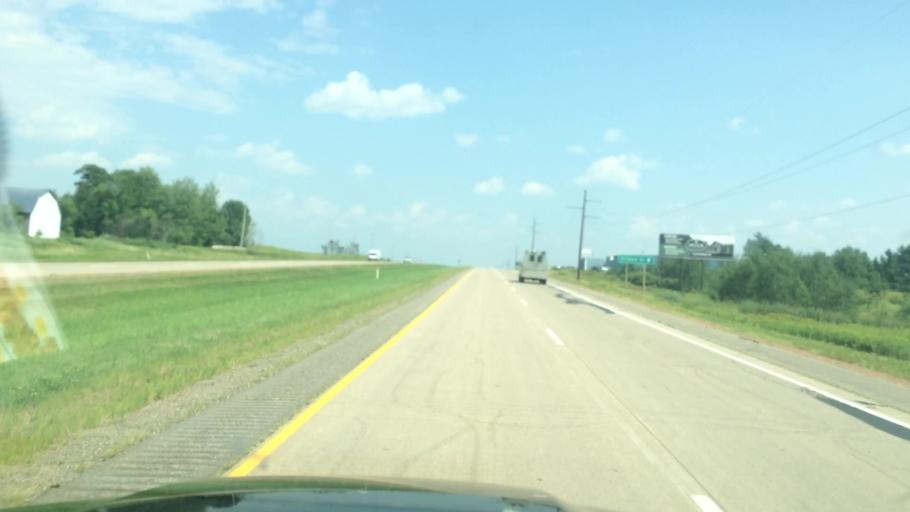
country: US
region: Wisconsin
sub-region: Marathon County
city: Edgar
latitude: 44.9441
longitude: -90.0095
